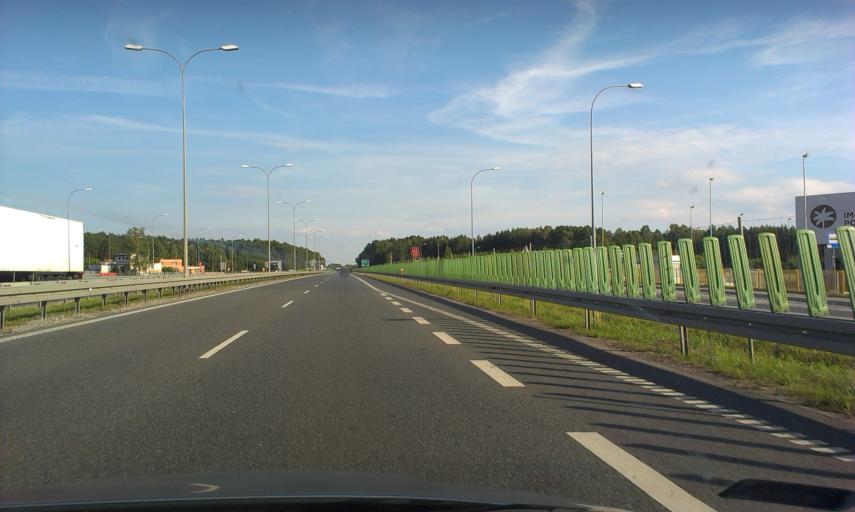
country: PL
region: Kujawsko-Pomorskie
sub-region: Powiat bydgoski
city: Biale Blota
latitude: 53.0874
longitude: 17.9035
